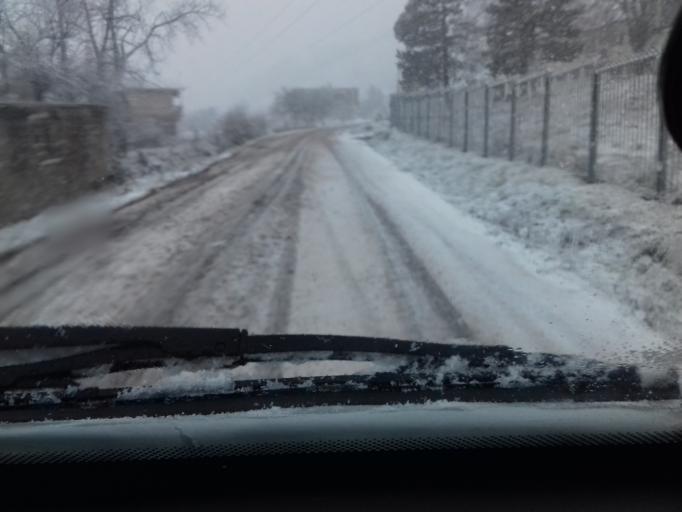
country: BA
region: Federation of Bosnia and Herzegovina
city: Lokvine
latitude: 44.2297
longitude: 17.8489
